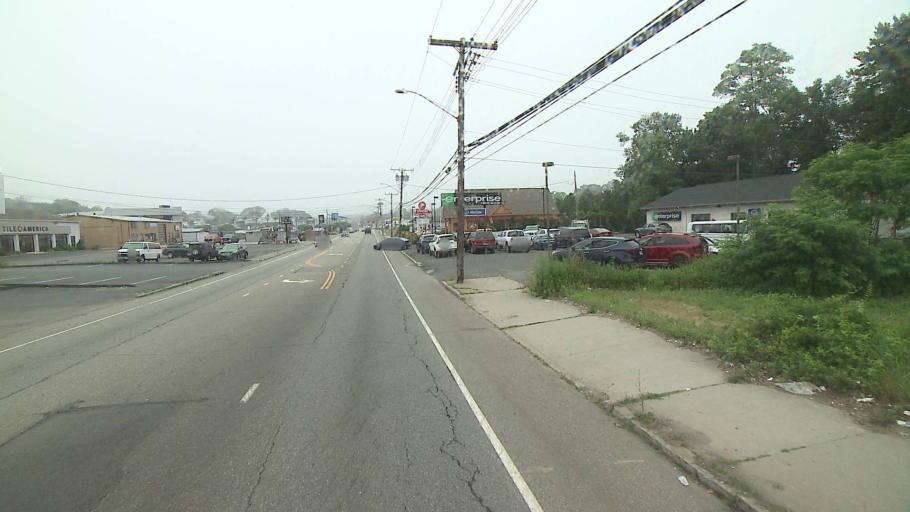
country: US
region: Connecticut
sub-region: New London County
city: New London
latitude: 41.3613
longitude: -72.1161
